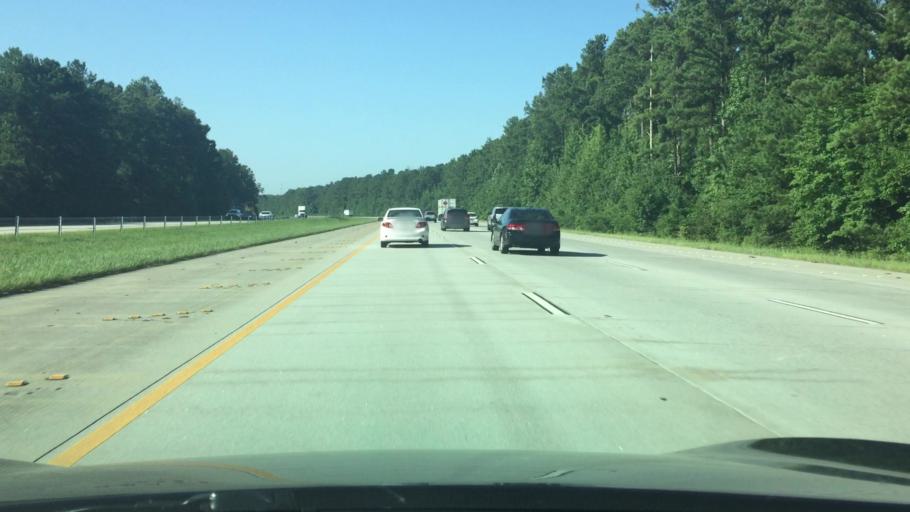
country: US
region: Georgia
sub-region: Coweta County
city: Grantville
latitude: 33.2695
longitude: -84.8040
